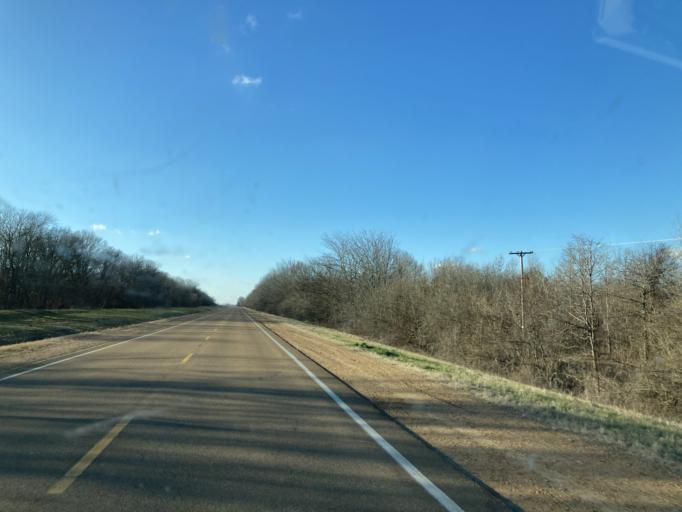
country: US
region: Mississippi
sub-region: Yazoo County
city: Yazoo City
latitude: 32.9199
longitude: -90.5602
